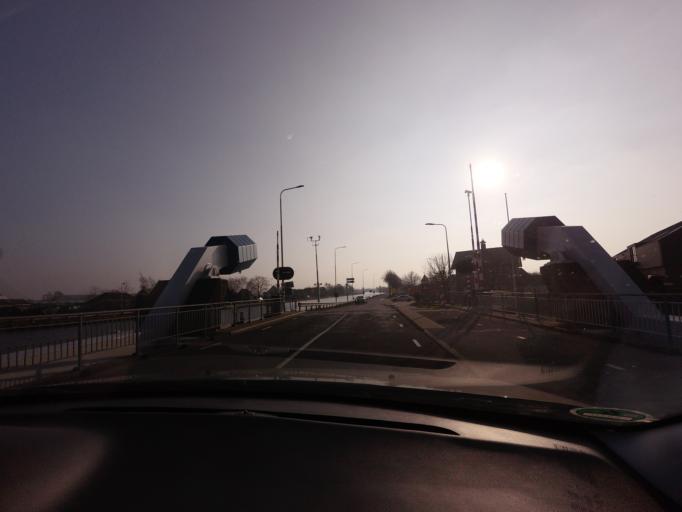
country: NL
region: South Holland
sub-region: Gemeente Nieuwkoop
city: Nieuwkoop
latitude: 52.1775
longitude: 4.7167
